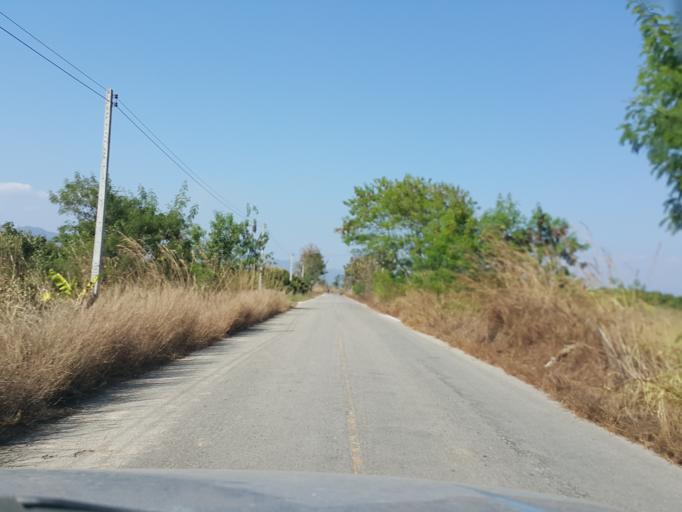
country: TH
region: Chiang Mai
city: Mae Wang
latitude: 18.5663
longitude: 98.7920
